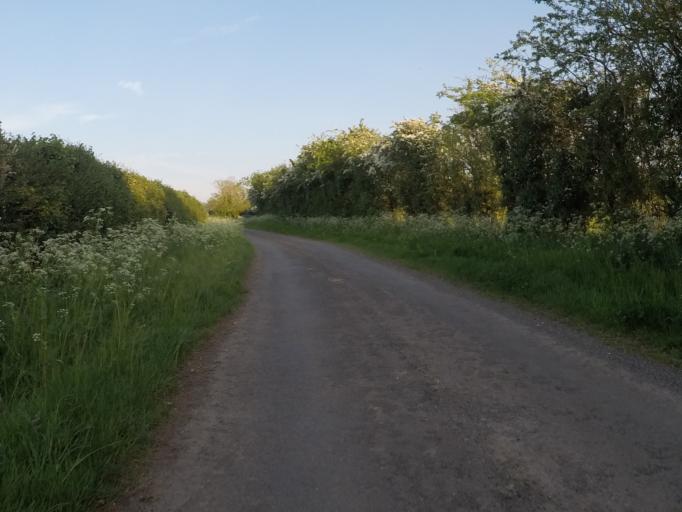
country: GB
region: England
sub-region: Oxfordshire
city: Shipton under Wychwood
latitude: 51.8571
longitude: -1.5515
